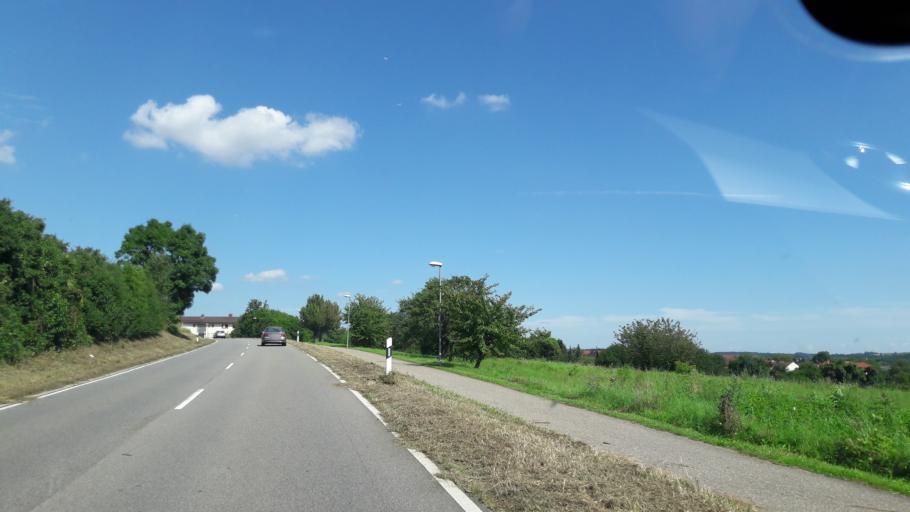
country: DE
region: Baden-Wuerttemberg
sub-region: Karlsruhe Region
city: Malsch
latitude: 49.2428
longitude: 8.6671
